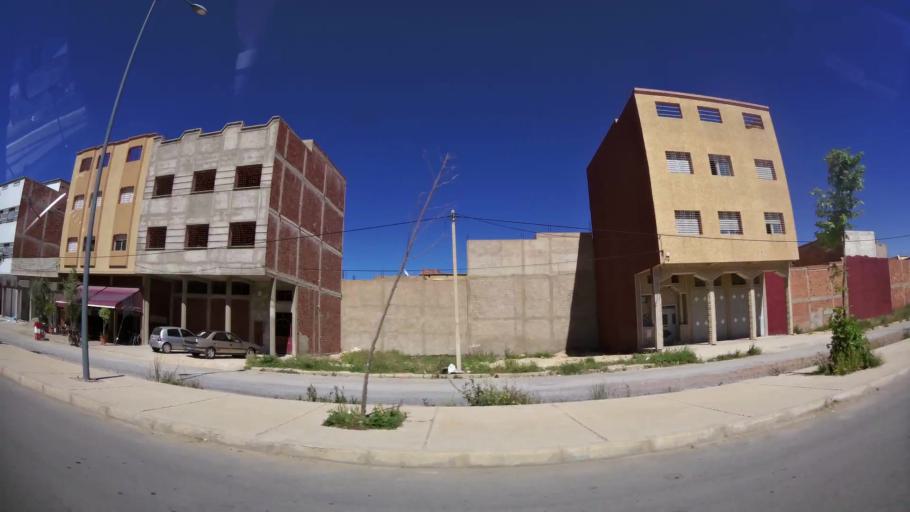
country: MA
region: Oriental
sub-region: Oujda-Angad
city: Oujda
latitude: 34.6746
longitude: -1.8596
